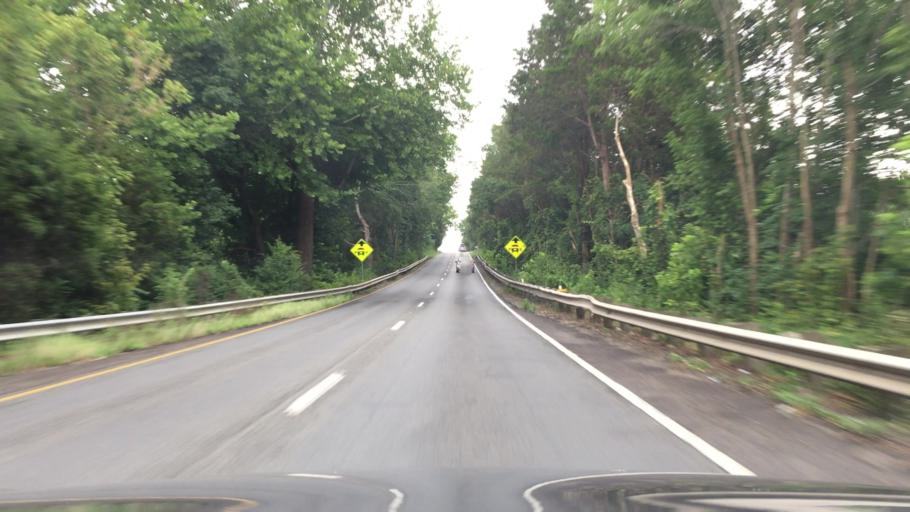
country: US
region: Virginia
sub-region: Spotsylvania County
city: Spotsylvania
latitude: 38.3252
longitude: -77.7254
